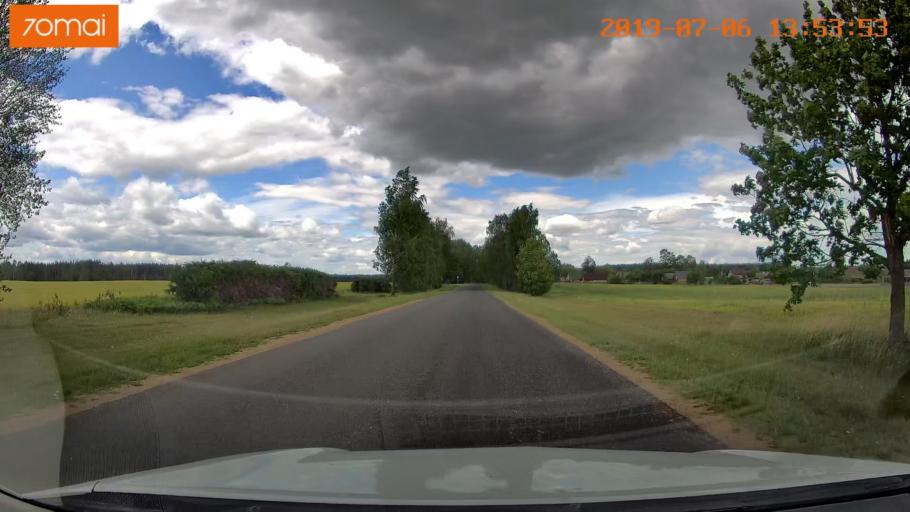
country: BY
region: Minsk
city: Ivyanyets
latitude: 53.7395
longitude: 26.8232
